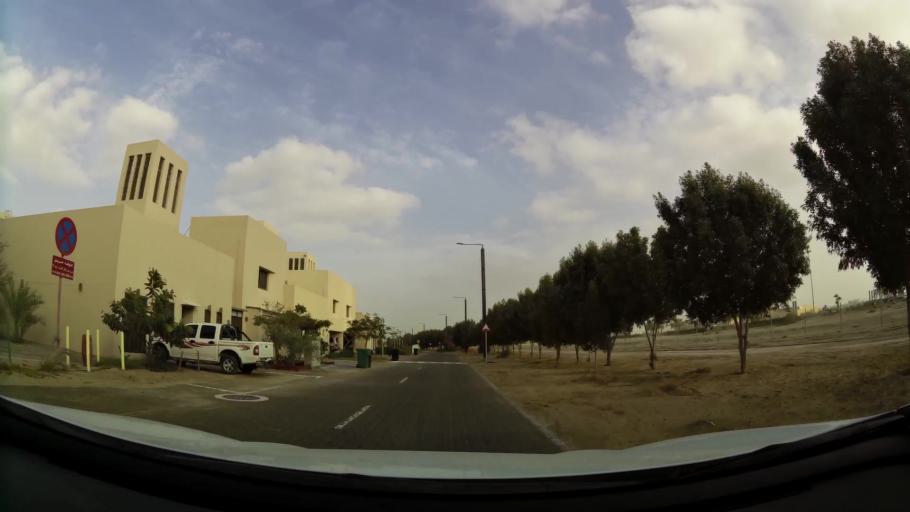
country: AE
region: Abu Dhabi
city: Abu Dhabi
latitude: 24.5005
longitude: 54.5954
